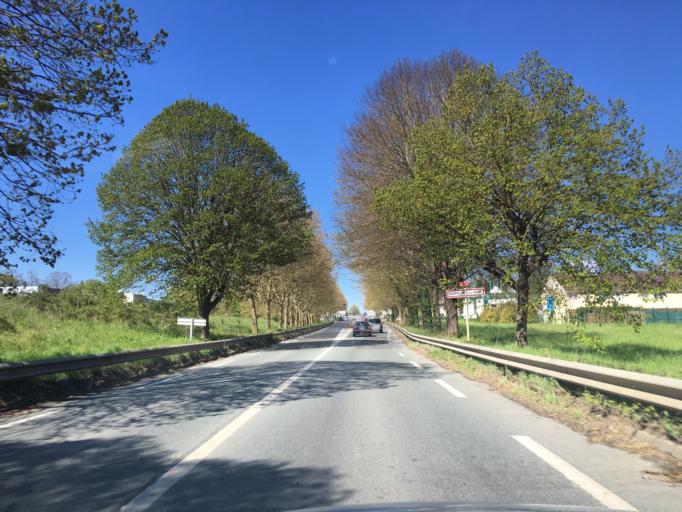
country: FR
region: Ile-de-France
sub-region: Departement du Val-de-Marne
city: Villecresnes
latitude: 48.7277
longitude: 2.5428
